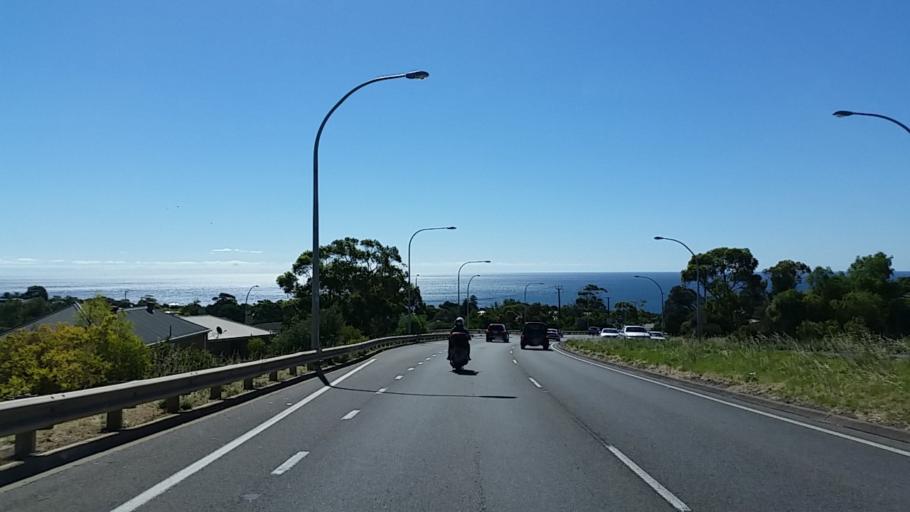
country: AU
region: South Australia
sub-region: Adelaide Hills
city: Seacliff
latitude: -35.0405
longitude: 138.5278
